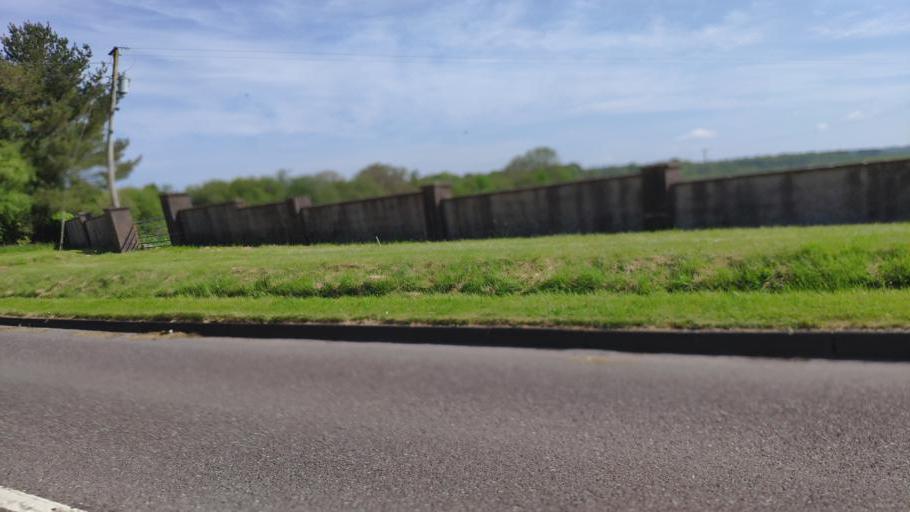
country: IE
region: Munster
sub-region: County Cork
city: Blarney
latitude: 51.9271
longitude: -8.5571
